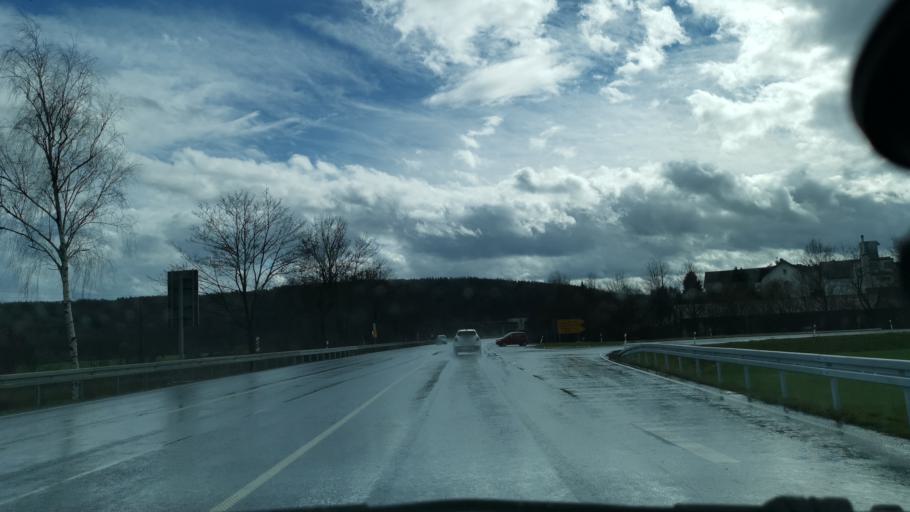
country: DE
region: Hesse
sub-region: Regierungsbezirk Kassel
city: Bad Hersfeld
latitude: 50.9061
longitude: 9.7488
